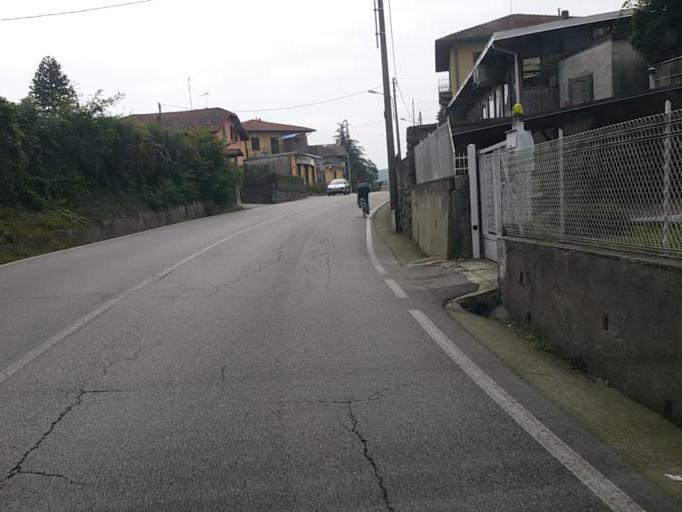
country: IT
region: Piedmont
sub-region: Provincia di Novara
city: Bolzano Novarese
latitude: 45.7571
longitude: 8.4318
